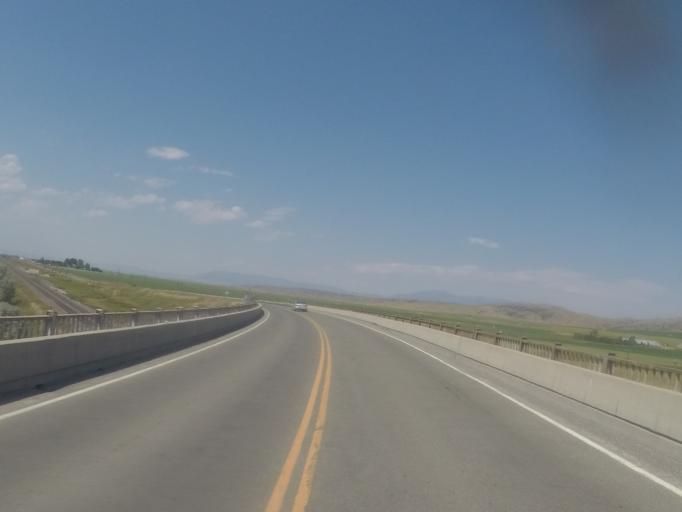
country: US
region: Montana
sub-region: Broadwater County
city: Townsend
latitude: 46.1771
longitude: -111.4440
